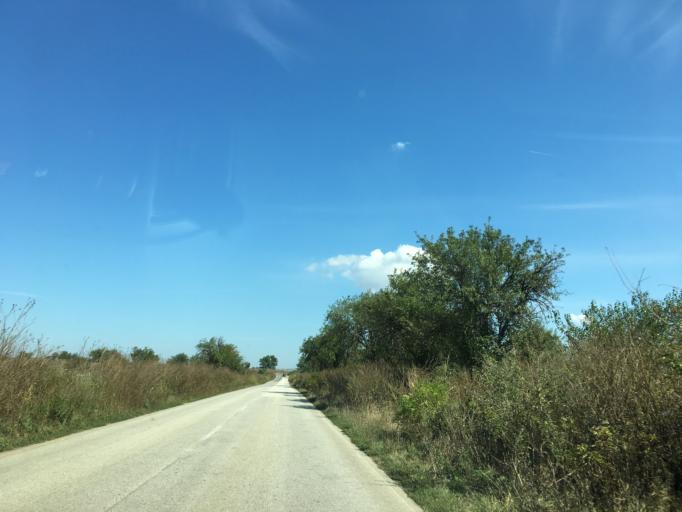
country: RO
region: Olt
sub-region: Comuna Orlea
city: Orlea
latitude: 43.6076
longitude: 24.3610
